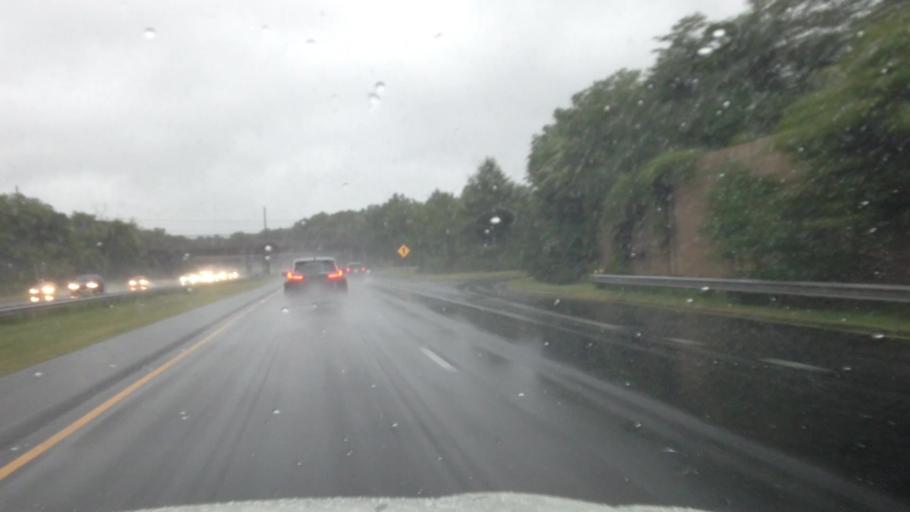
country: US
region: Maryland
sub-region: Prince George's County
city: Landover
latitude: 38.9318
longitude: -76.8957
